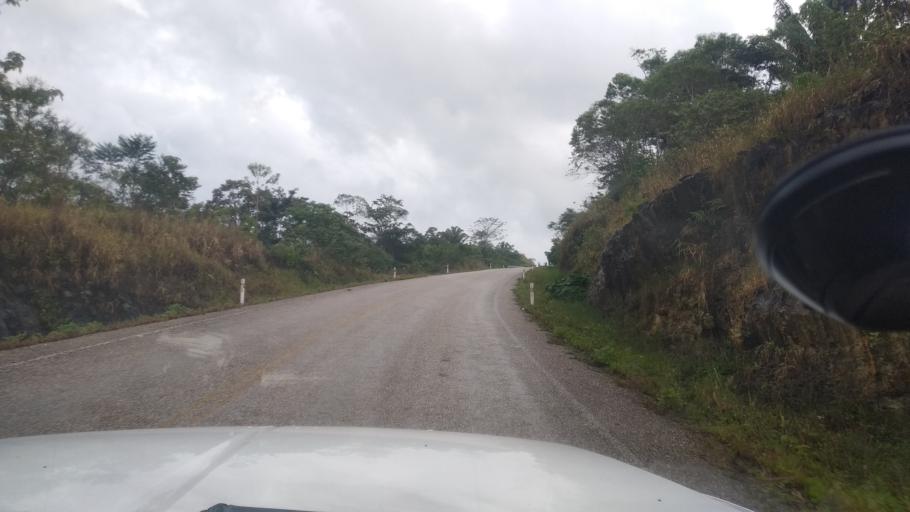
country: GT
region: Peten
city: San Luis
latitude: 16.1941
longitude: -89.1700
